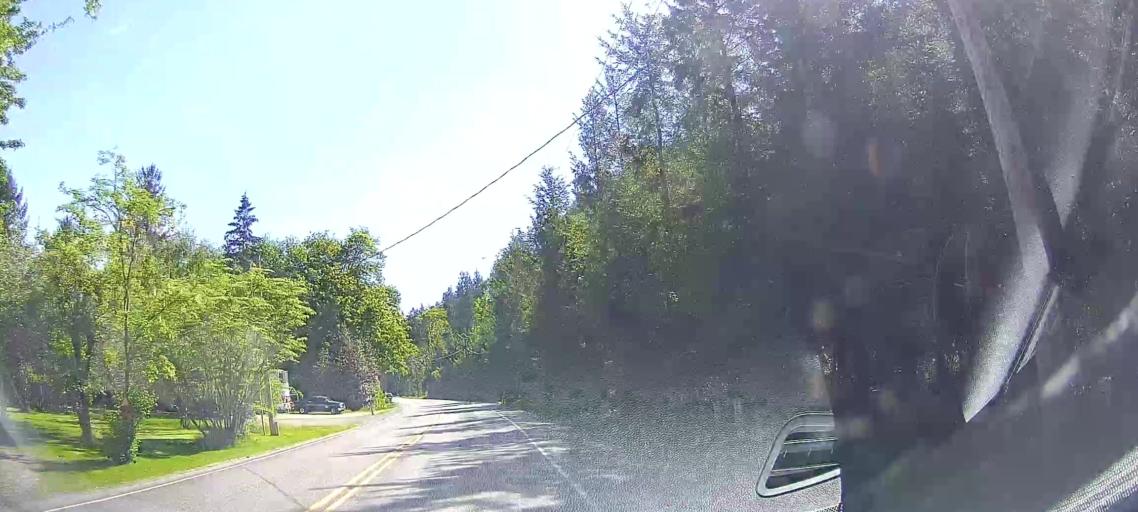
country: US
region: Washington
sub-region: Skagit County
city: Sedro-Woolley
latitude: 48.4870
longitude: -122.2196
